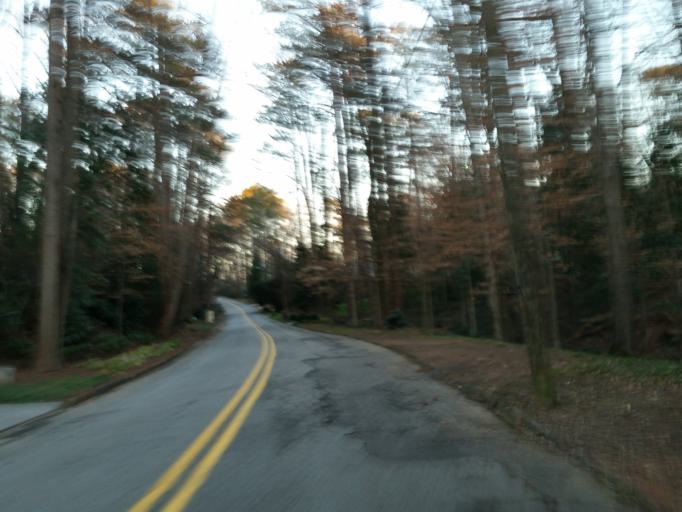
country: US
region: Georgia
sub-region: Cobb County
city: Vinings
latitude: 33.8424
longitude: -84.4498
